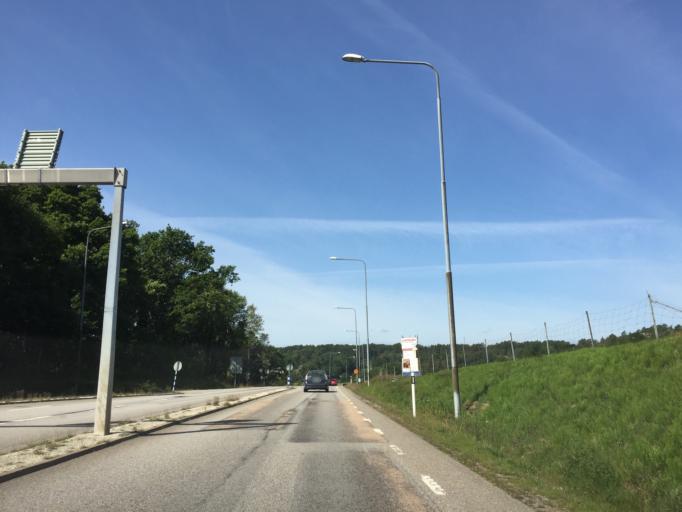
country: SE
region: Vaestra Goetaland
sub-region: Lysekils Kommun
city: Lysekil
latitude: 58.3028
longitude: 11.5006
